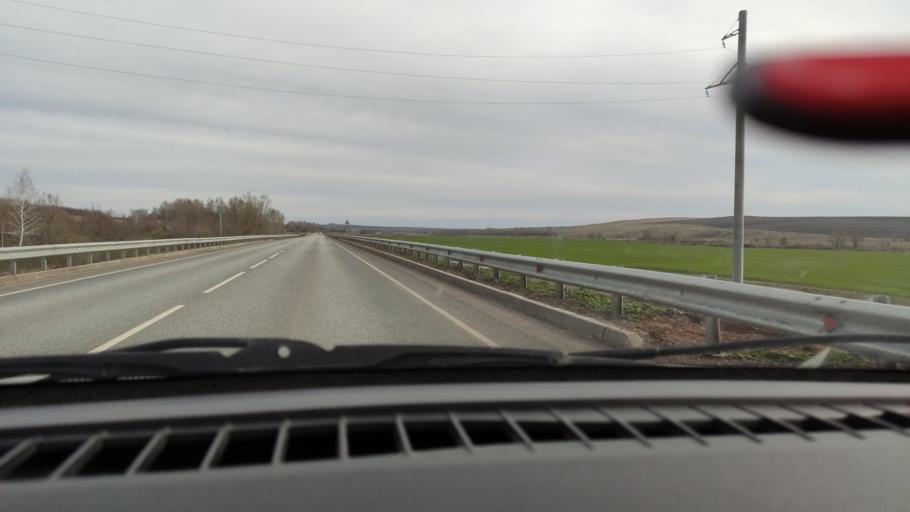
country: RU
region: Bashkortostan
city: Yermolayevo
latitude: 52.6309
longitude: 55.8431
